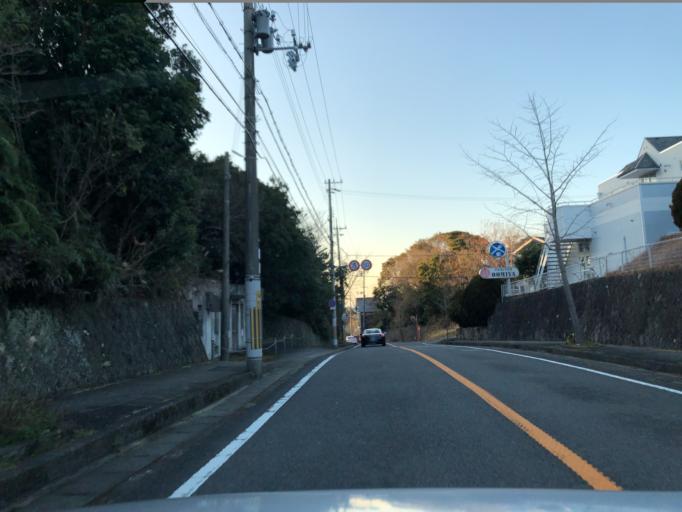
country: JP
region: Wakayama
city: Tanabe
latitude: 33.6681
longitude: 135.3673
